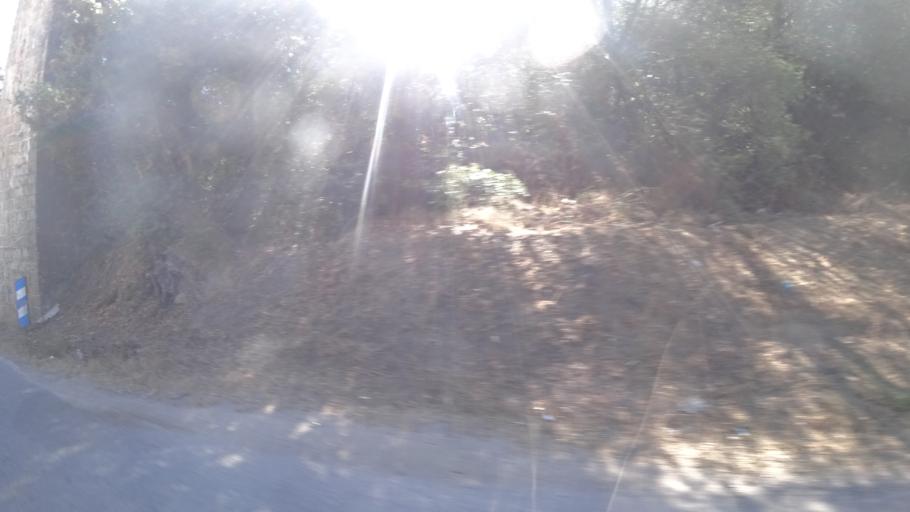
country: FR
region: Corsica
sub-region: Departement de la Corse-du-Sud
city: Ajaccio
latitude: 41.9442
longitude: 8.7350
